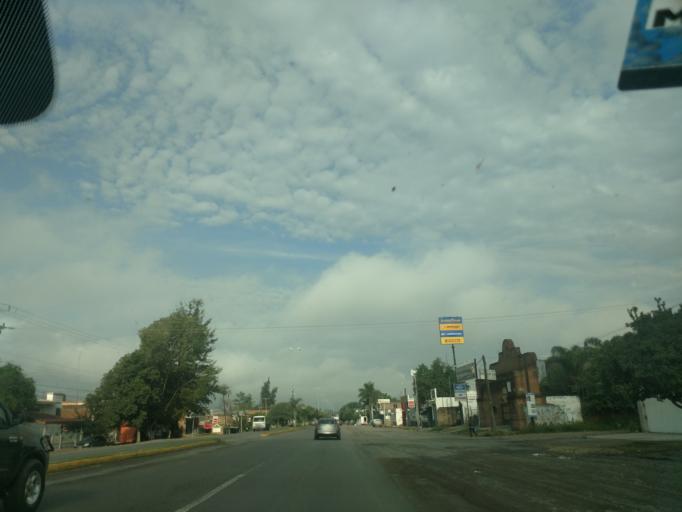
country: MX
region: Jalisco
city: Ameca
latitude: 20.5362
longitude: -104.0315
